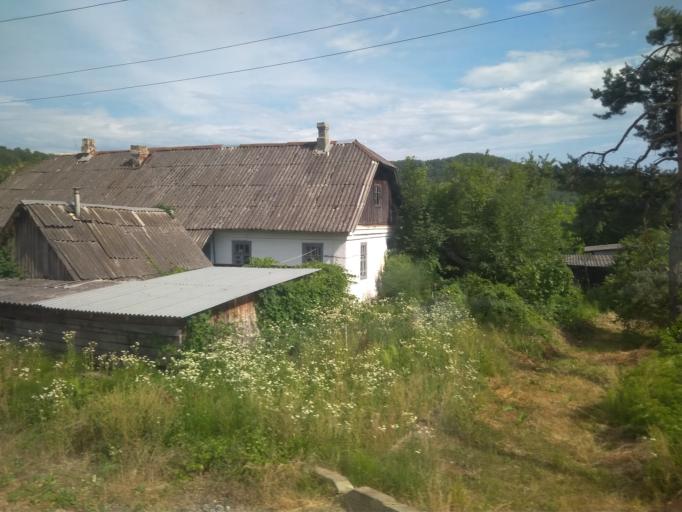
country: RU
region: Krasnodarskiy
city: Khadyzhensk
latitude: 44.4403
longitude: 39.4848
